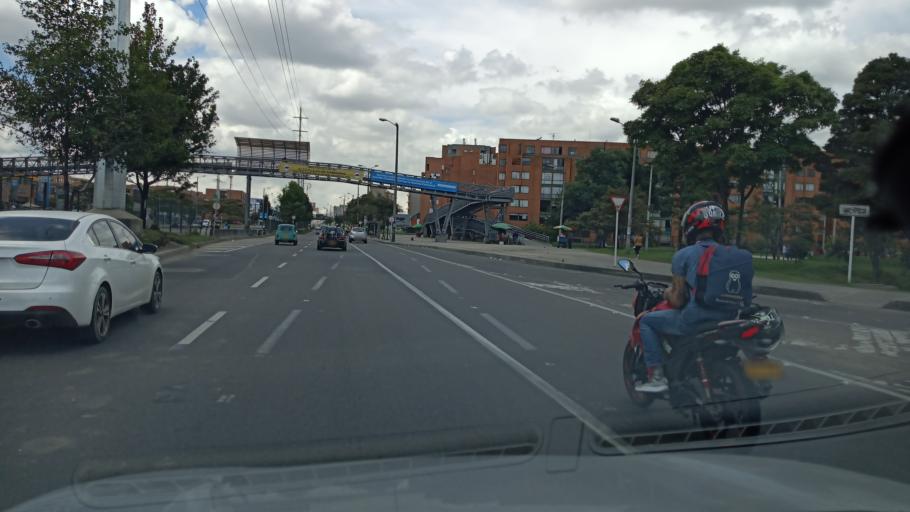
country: CO
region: Bogota D.C.
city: Bogota
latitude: 4.6648
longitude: -74.1315
